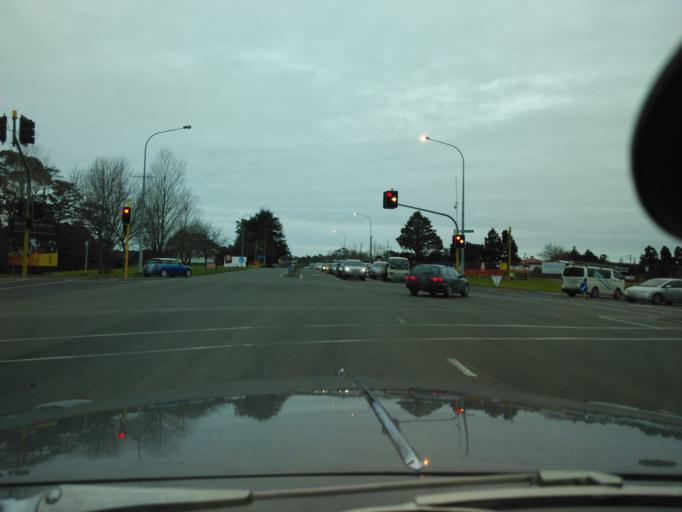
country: NZ
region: Auckland
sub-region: Auckland
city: Rothesay Bay
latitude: -36.7269
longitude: 174.6978
